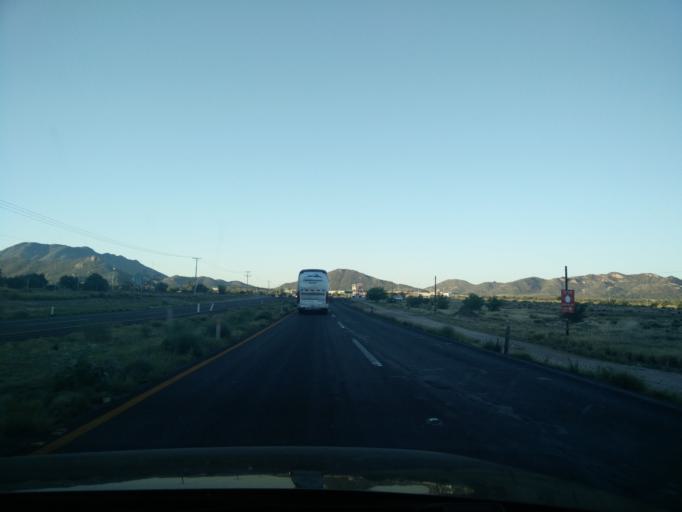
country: MX
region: Sonora
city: Hermosillo
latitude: 29.0195
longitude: -110.9614
